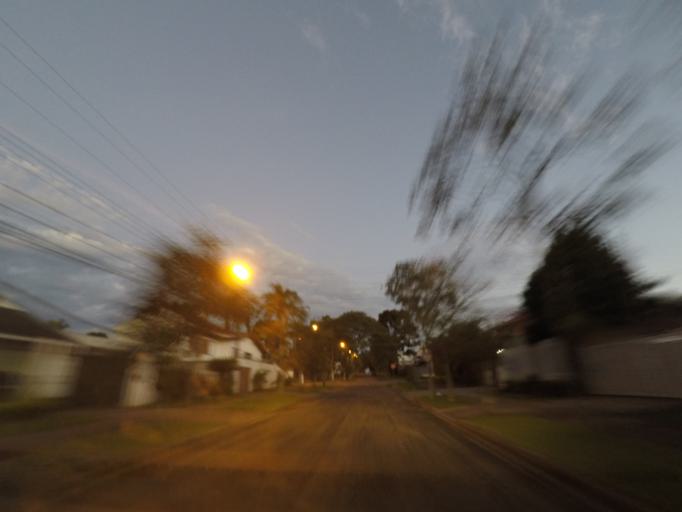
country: BR
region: Parana
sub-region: Curitiba
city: Curitiba
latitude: -25.4169
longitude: -49.2398
